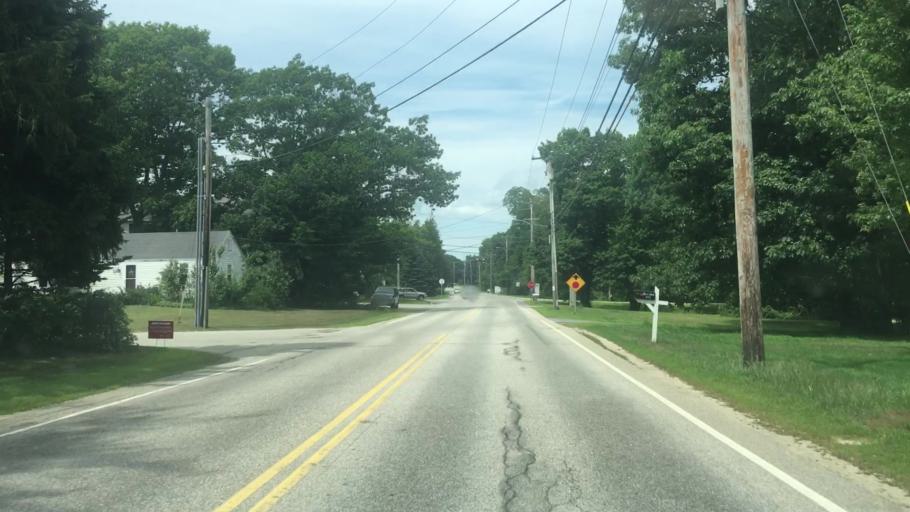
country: US
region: Maine
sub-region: Cumberland County
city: Scarborough
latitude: 43.5899
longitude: -70.2954
